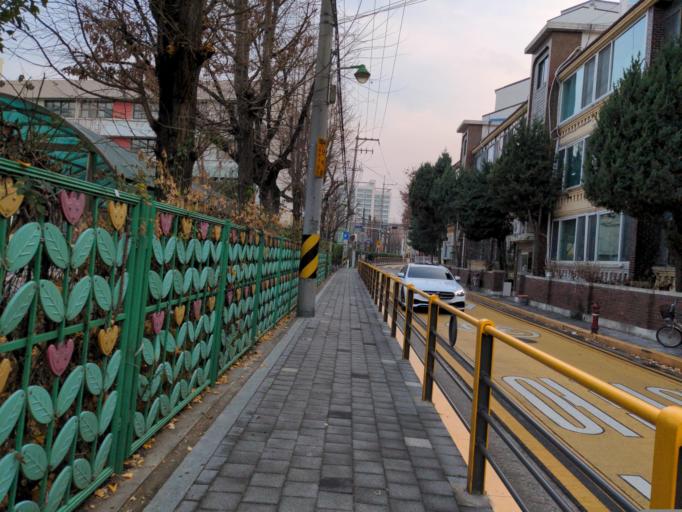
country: KR
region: Seoul
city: Seoul
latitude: 37.5401
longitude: 127.0577
